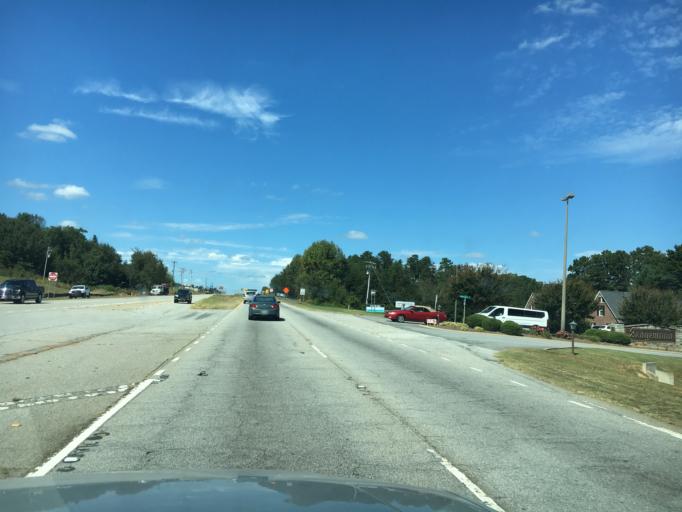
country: US
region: South Carolina
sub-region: Anderson County
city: Powdersville
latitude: 34.8085
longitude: -82.5137
